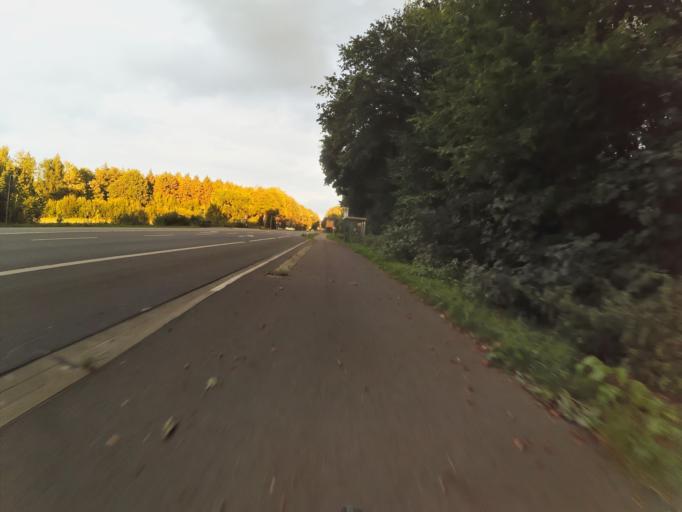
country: DE
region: North Rhine-Westphalia
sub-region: Regierungsbezirk Munster
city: Mettingen
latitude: 52.2828
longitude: 7.7796
